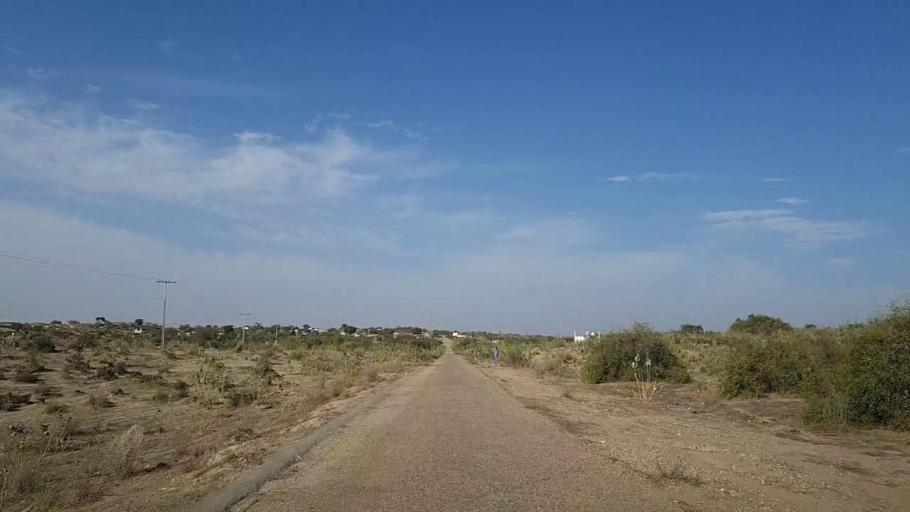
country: PK
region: Sindh
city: Naukot
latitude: 24.8604
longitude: 69.5262
